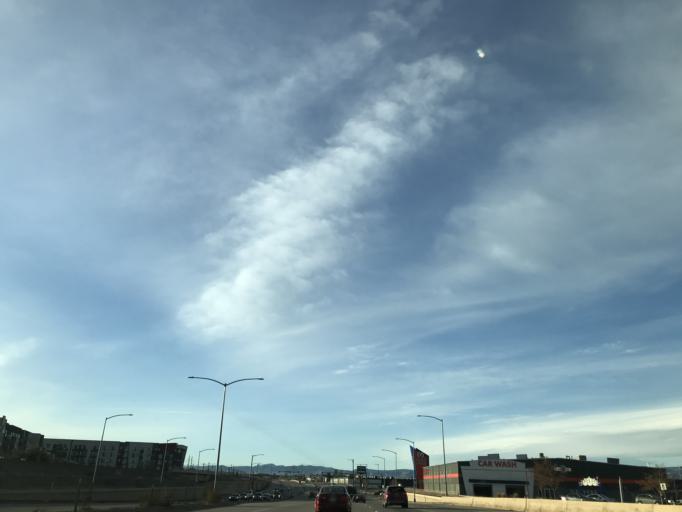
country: US
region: Colorado
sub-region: Arapahoe County
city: Englewood
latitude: 39.6441
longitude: -105.0052
